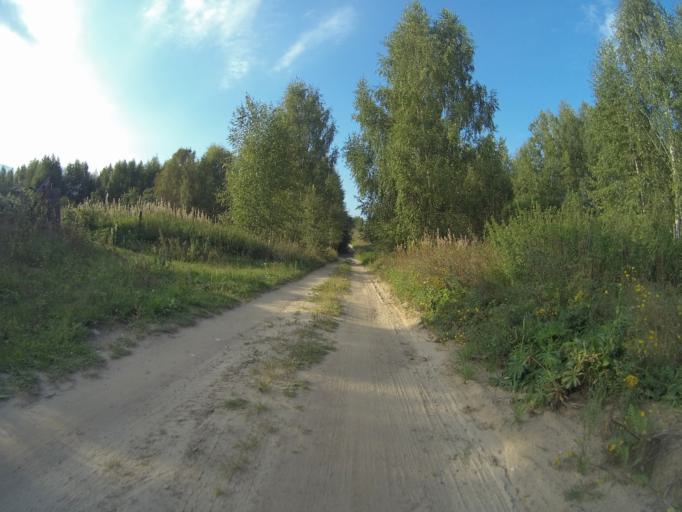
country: RU
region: Vladimir
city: Raduzhnyy
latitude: 55.9951
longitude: 40.3722
